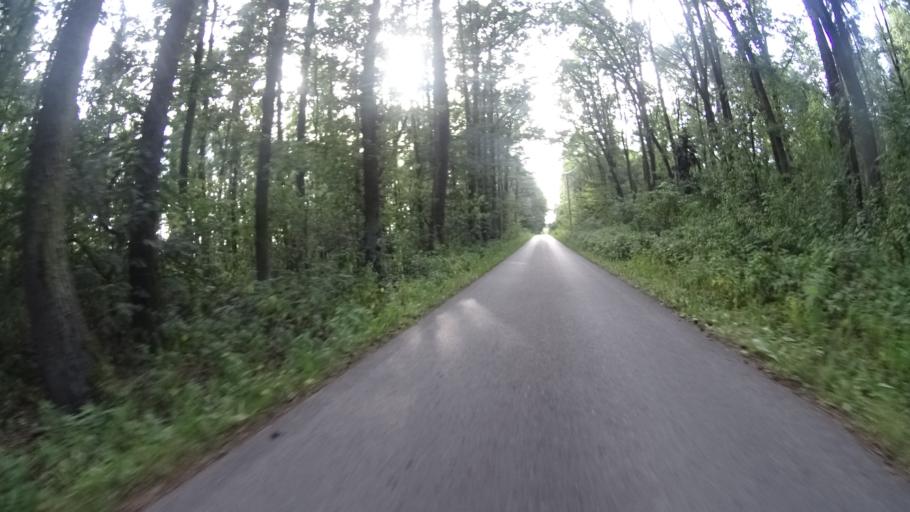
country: PL
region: Masovian Voivodeship
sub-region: Powiat bialobrzeski
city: Wysmierzyce
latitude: 51.6754
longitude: 20.8038
